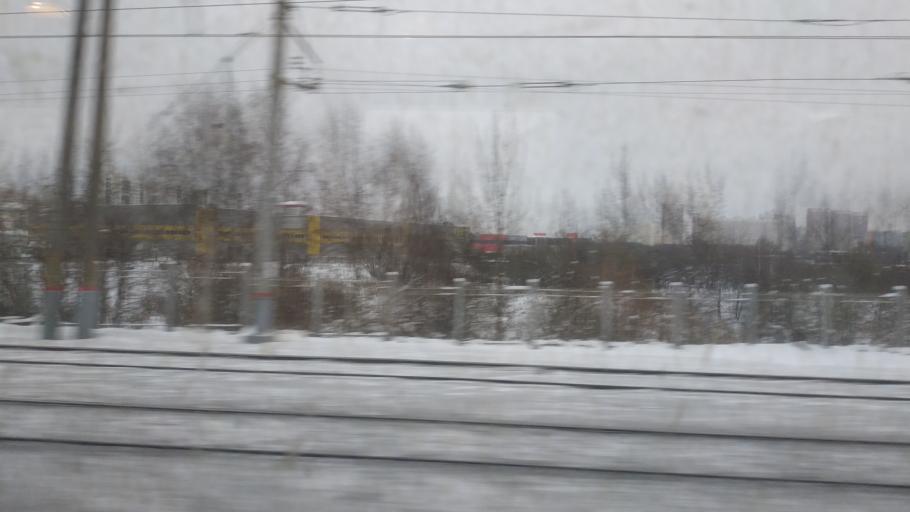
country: RU
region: Moskovskaya
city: Shcherbinka
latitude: 55.5345
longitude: 37.5693
